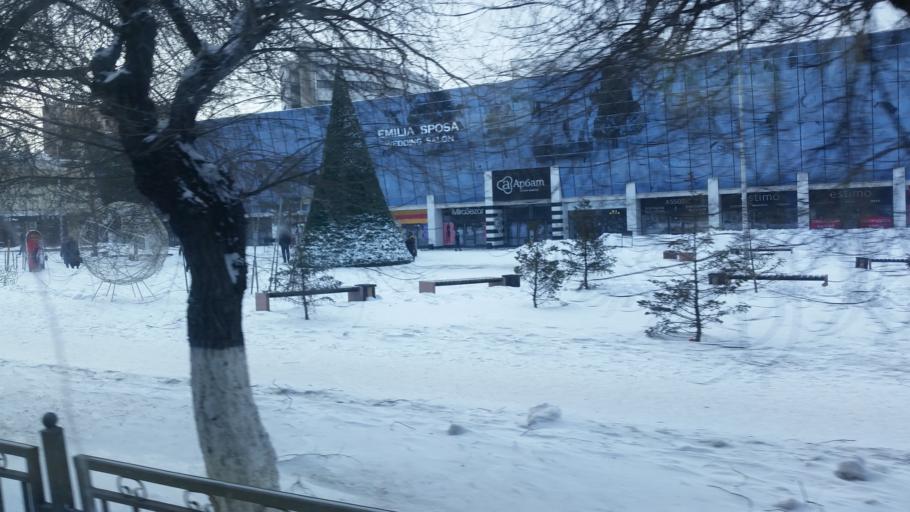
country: KZ
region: Qaraghandy
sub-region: Qaraghandy Qalasy
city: Karagandy
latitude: 49.8032
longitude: 73.0874
